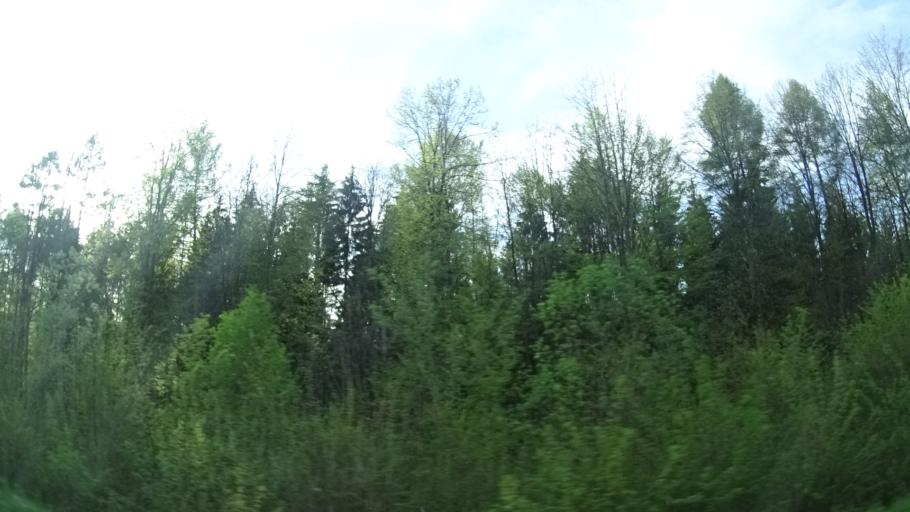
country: DE
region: Baden-Wuerttemberg
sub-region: Karlsruhe Region
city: Limbach
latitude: 49.4928
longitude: 9.2593
